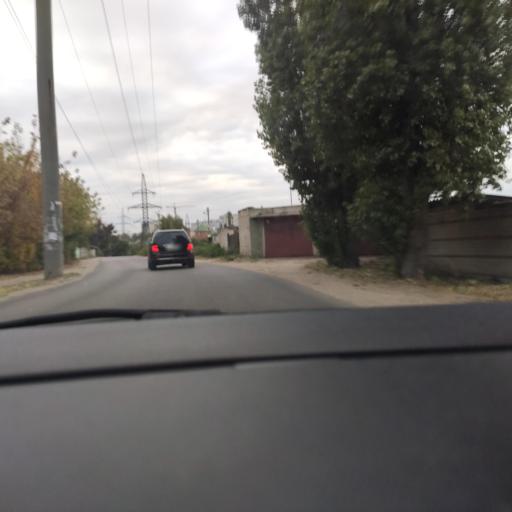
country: RU
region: Voronezj
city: Voronezh
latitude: 51.6883
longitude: 39.2059
